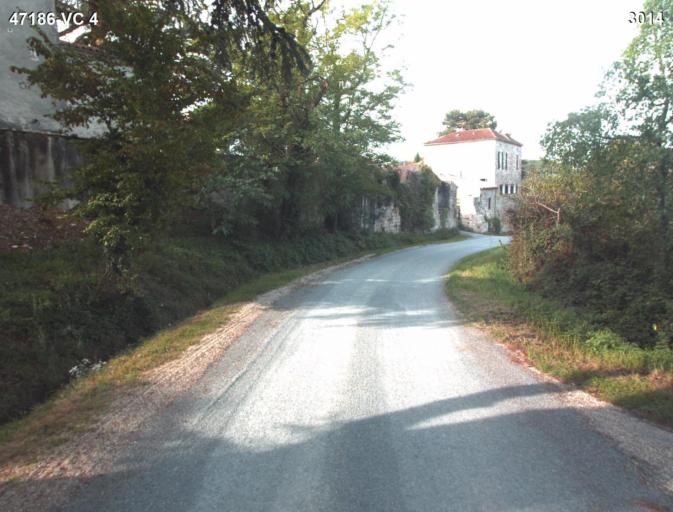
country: FR
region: Aquitaine
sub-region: Departement du Lot-et-Garonne
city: Port-Sainte-Marie
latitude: 44.2026
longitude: 0.4419
